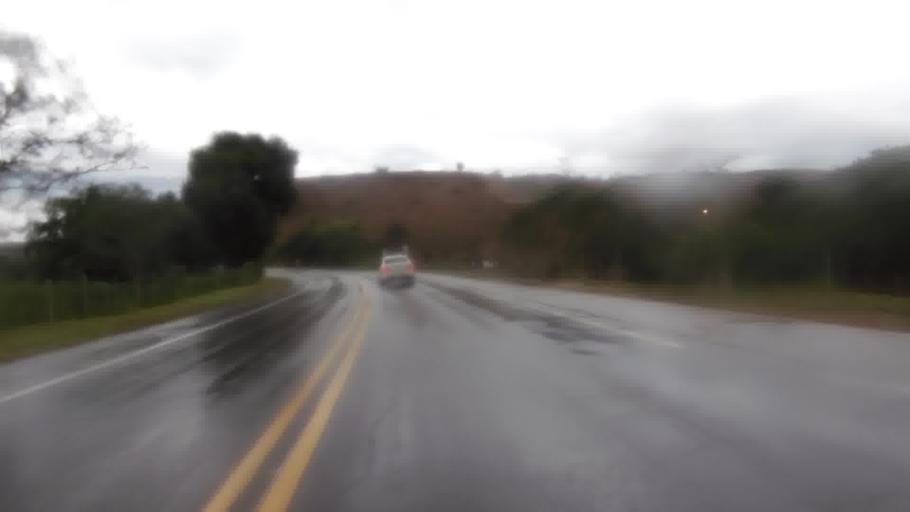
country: BR
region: Espirito Santo
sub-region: Cachoeiro De Itapemirim
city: Cachoeiro de Itapemirim
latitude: -20.9826
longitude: -41.1186
